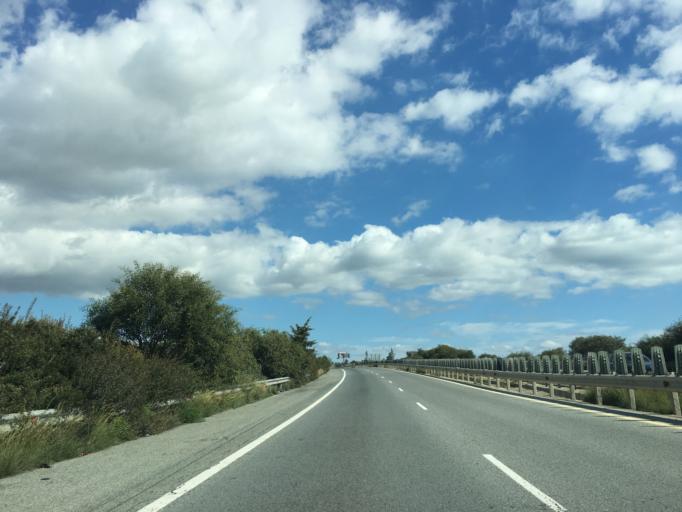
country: CY
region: Limassol
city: Pyrgos
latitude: 34.7300
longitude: 33.2790
